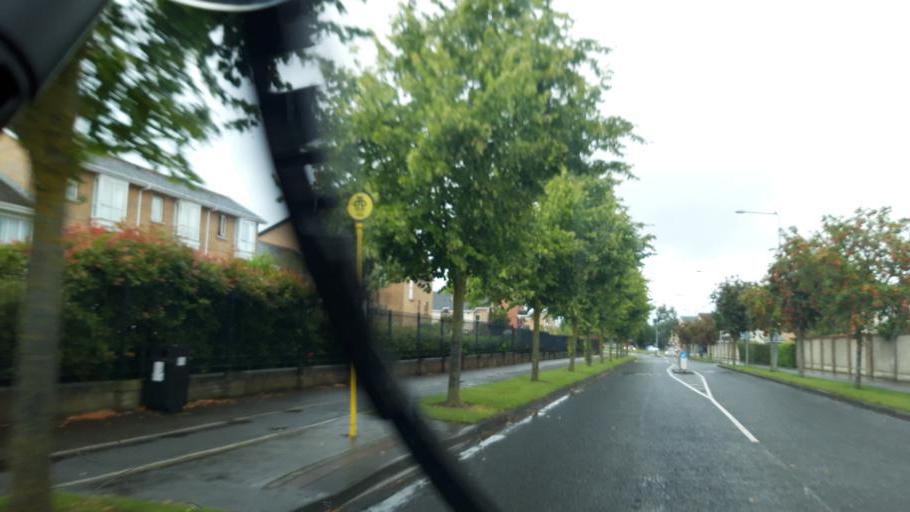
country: IE
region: Leinster
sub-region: Fingal County
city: Blanchardstown
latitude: 53.3742
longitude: -6.4017
